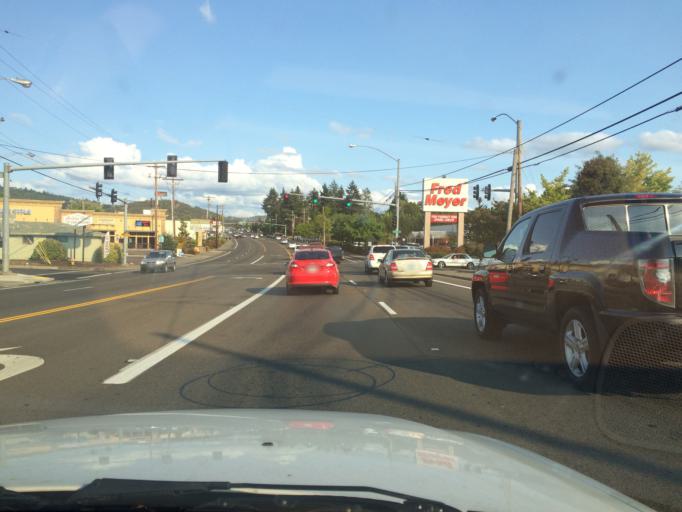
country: US
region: Oregon
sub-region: Douglas County
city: Roseburg
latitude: 43.2297
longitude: -123.3700
